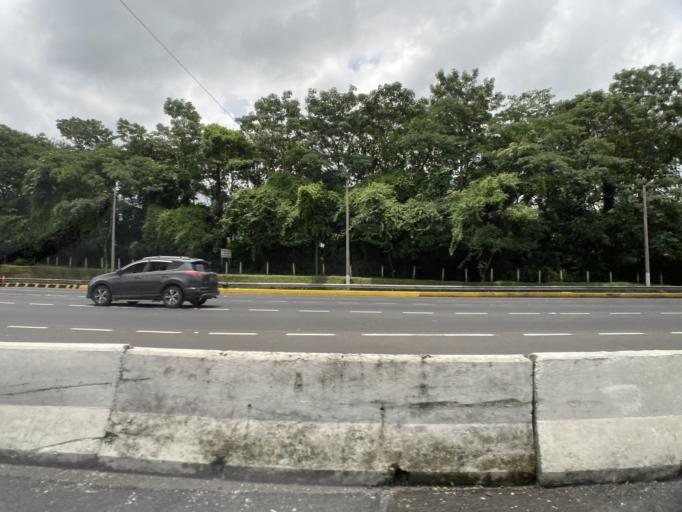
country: GT
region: Escuintla
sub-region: Municipio de Escuintla
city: Escuintla
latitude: 14.3603
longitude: -90.7855
